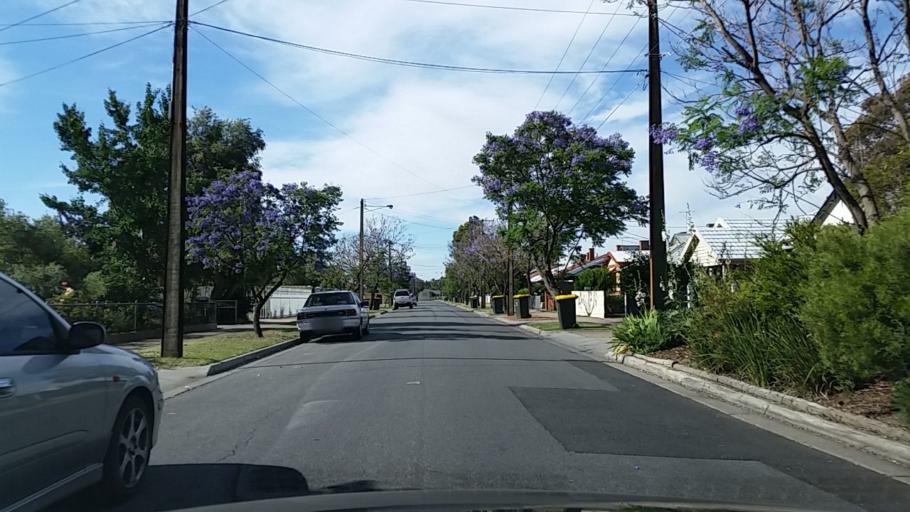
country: AU
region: South Australia
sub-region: Charles Sturt
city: Allenby Gardens
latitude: -34.9036
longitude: 138.5543
